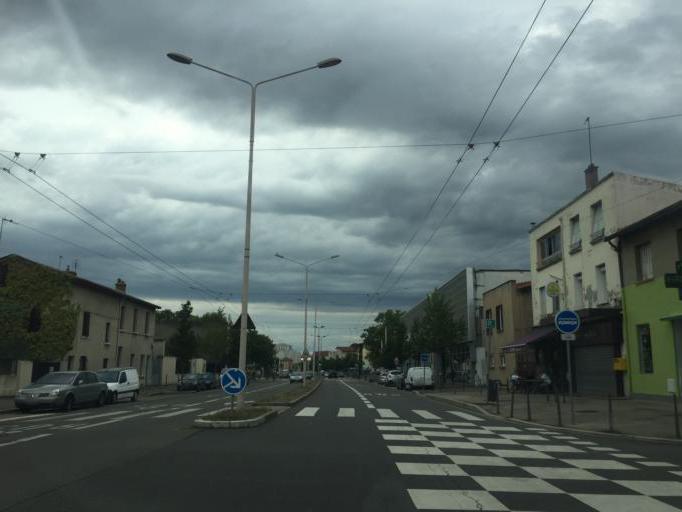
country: FR
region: Rhone-Alpes
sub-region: Departement du Rhone
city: Venissieux
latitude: 45.7236
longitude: 4.8840
